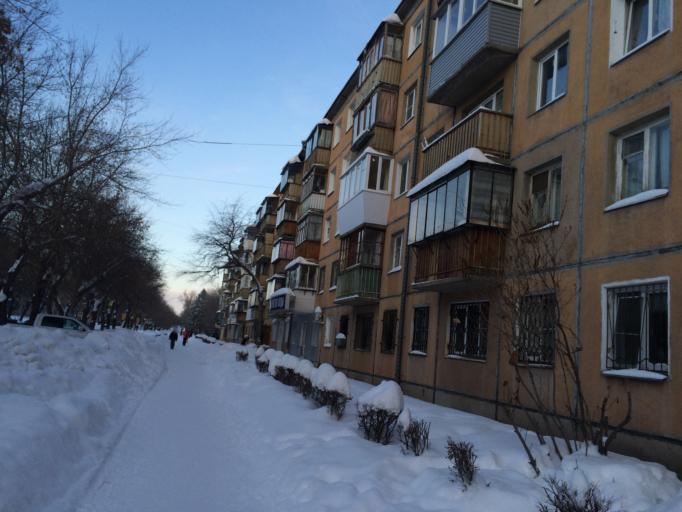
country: RU
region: Chelyabinsk
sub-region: Gorod Magnitogorsk
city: Magnitogorsk
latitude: 53.3996
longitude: 58.9717
